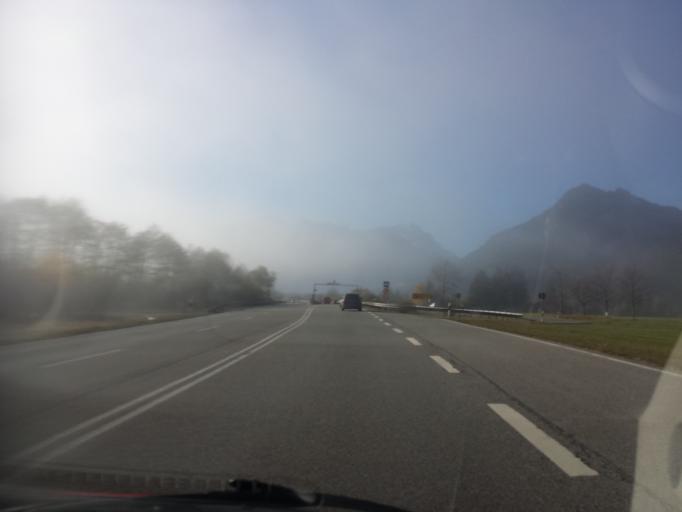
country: DE
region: Bavaria
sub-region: Upper Bavaria
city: Oberau
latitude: 47.5469
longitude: 11.1236
